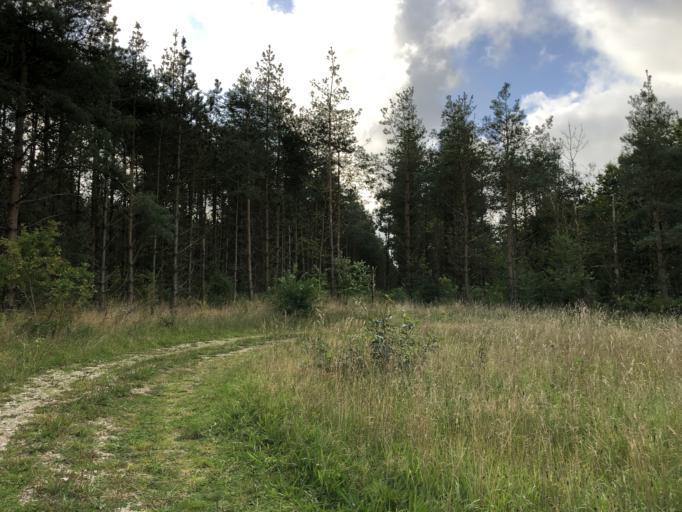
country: DK
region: Central Jutland
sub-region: Holstebro Kommune
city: Ulfborg
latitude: 56.3744
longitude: 8.3399
